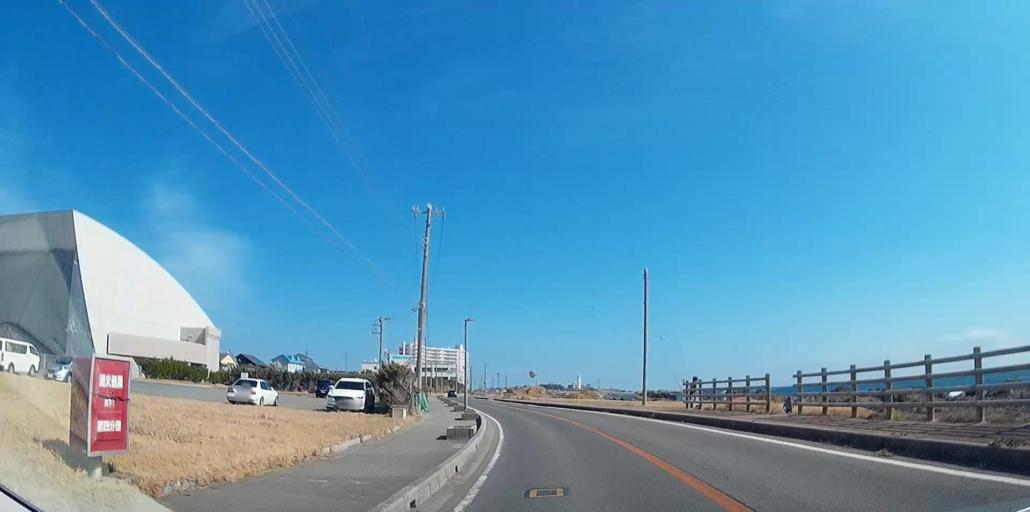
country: JP
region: Chiba
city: Tateyama
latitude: 34.9042
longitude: 139.8769
